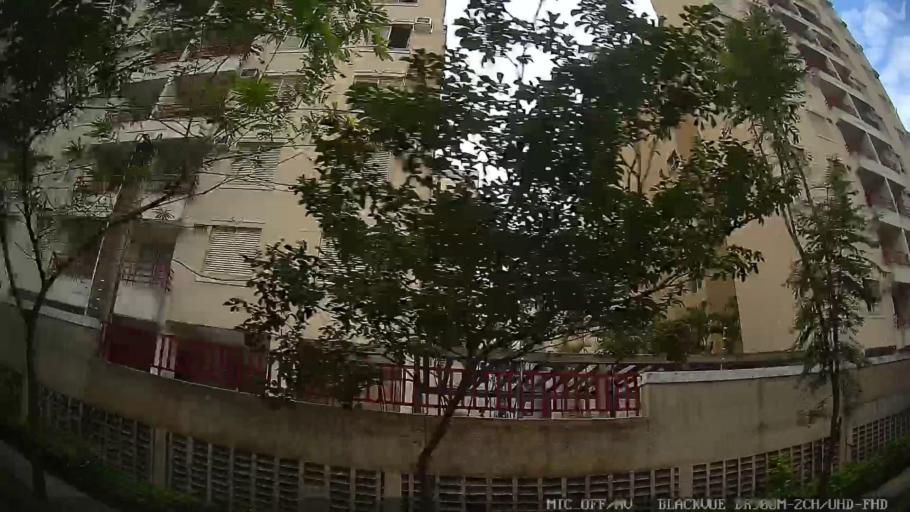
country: BR
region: Sao Paulo
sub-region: Guaruja
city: Guaruja
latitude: -23.9847
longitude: -46.2416
